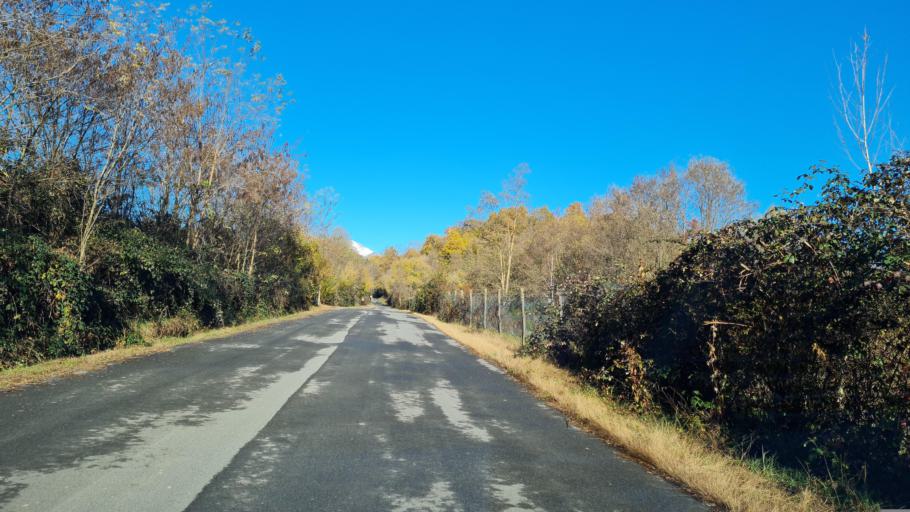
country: IT
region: Piedmont
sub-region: Provincia di Biella
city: Curino
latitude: 45.6117
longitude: 8.2387
